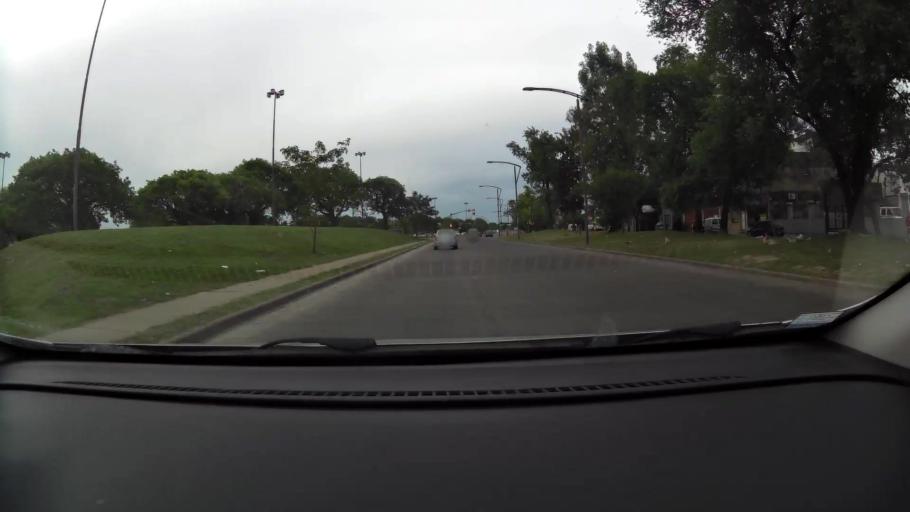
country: AR
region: Santa Fe
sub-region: Departamento de Rosario
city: Rosario
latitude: -32.9151
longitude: -60.6912
